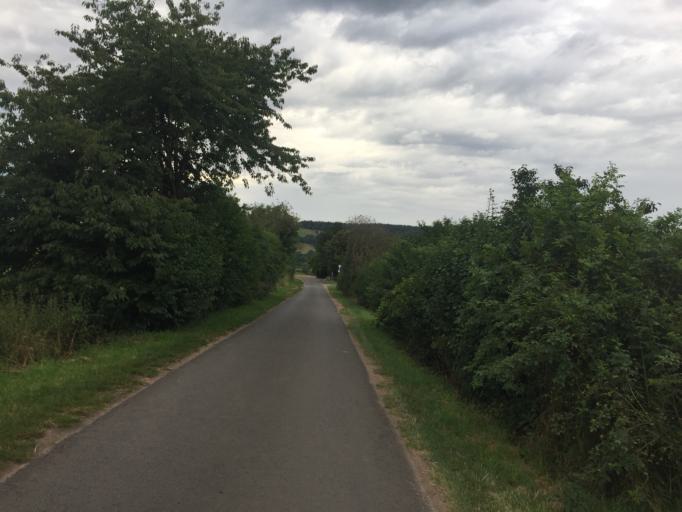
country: DE
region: Hesse
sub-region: Regierungsbezirk Kassel
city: Alheim
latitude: 51.0470
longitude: 9.6599
